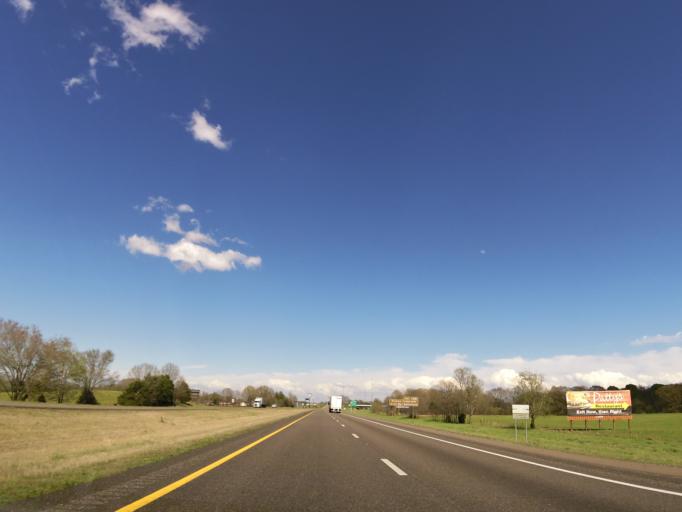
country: US
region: Tennessee
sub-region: Henderson County
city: Lexington
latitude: 35.7865
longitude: -88.4007
